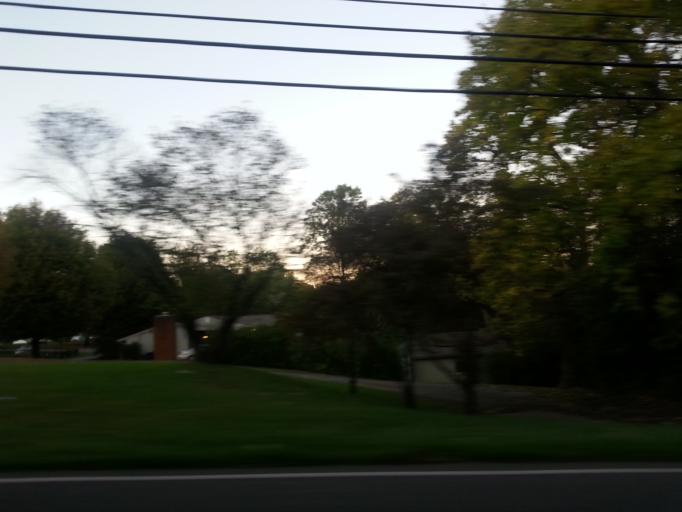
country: US
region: Tennessee
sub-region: Knox County
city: Knoxville
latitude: 36.0145
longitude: -83.9747
